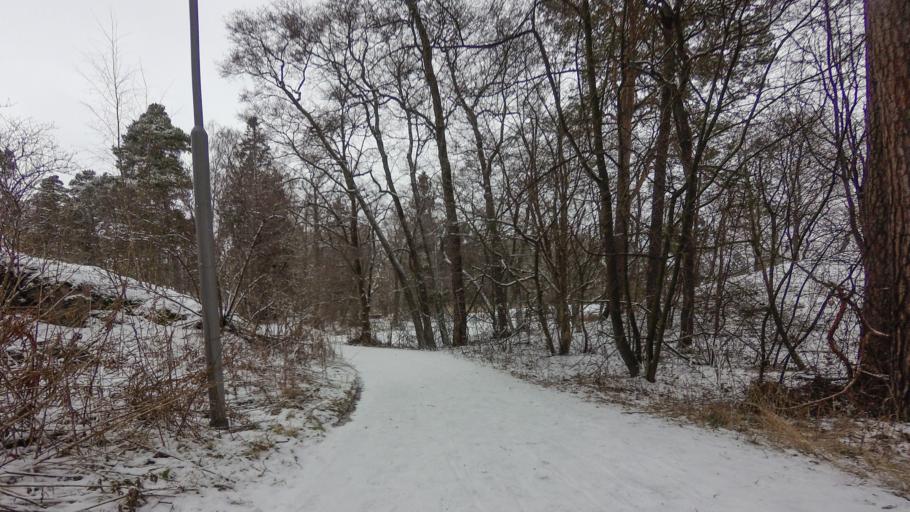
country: FI
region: Uusimaa
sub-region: Helsinki
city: Helsinki
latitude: 60.1769
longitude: 24.8868
